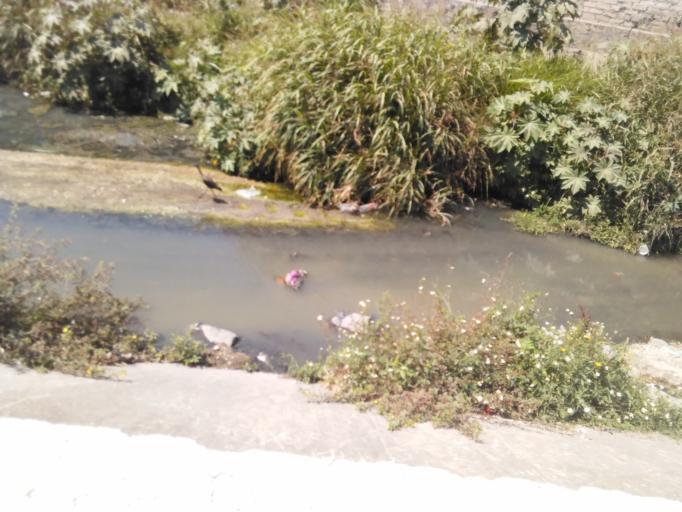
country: MX
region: Nayarit
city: Tepic
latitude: 21.4886
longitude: -104.8750
